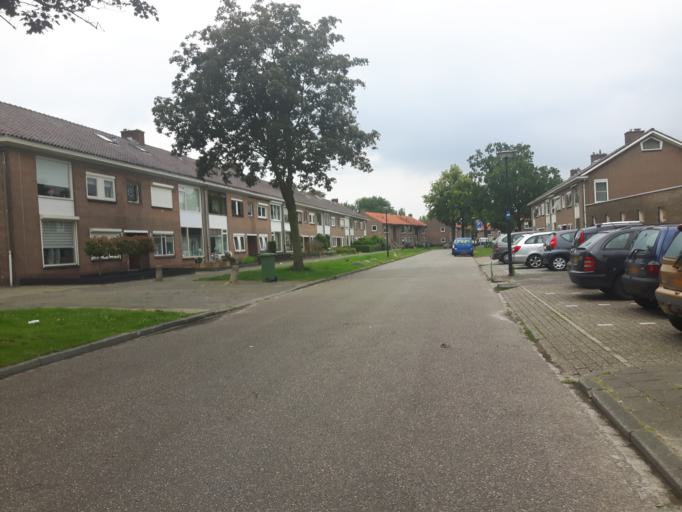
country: NL
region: Overijssel
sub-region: Gemeente Enschede
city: Enschede
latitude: 52.2119
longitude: 6.8647
